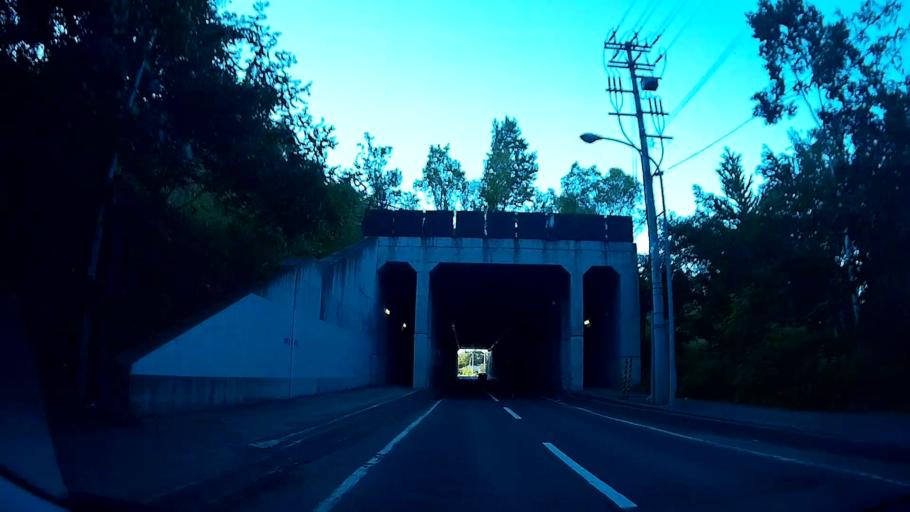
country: JP
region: Hokkaido
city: Otaru
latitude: 43.1586
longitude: 141.0414
